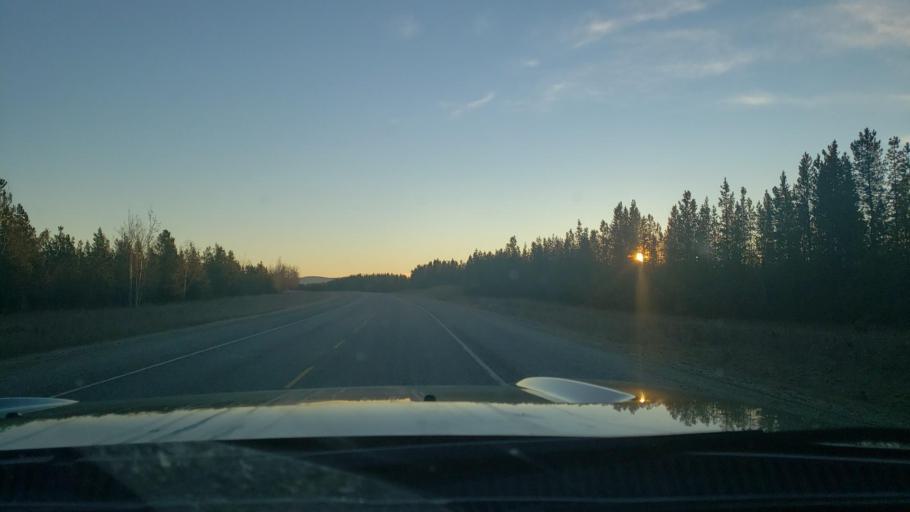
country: CA
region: Yukon
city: Watson Lake
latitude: 59.9293
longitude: -128.3784
